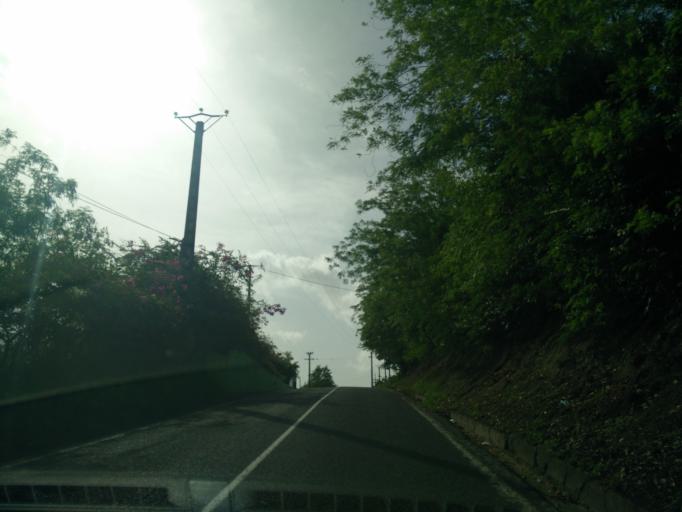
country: MQ
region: Martinique
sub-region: Martinique
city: Saint-Pierre
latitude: 14.7654
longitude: -61.1946
